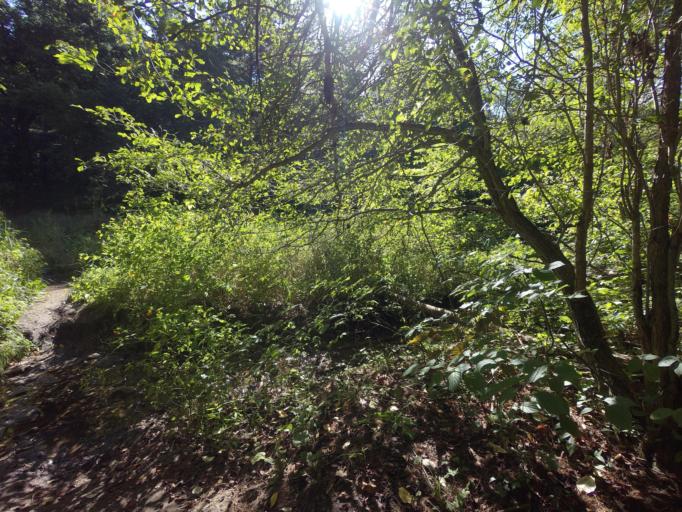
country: CA
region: Ontario
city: Waterloo
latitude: 43.6805
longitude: -80.4408
